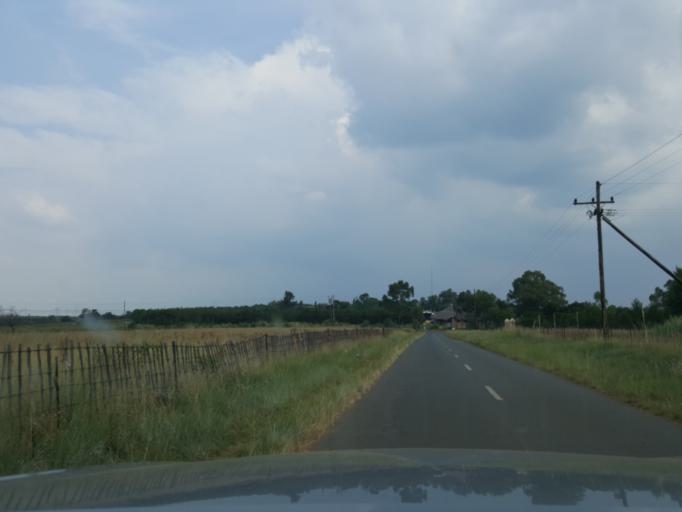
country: ZA
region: Gauteng
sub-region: City of Tshwane Metropolitan Municipality
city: Centurion
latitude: -25.8691
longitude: 28.3323
